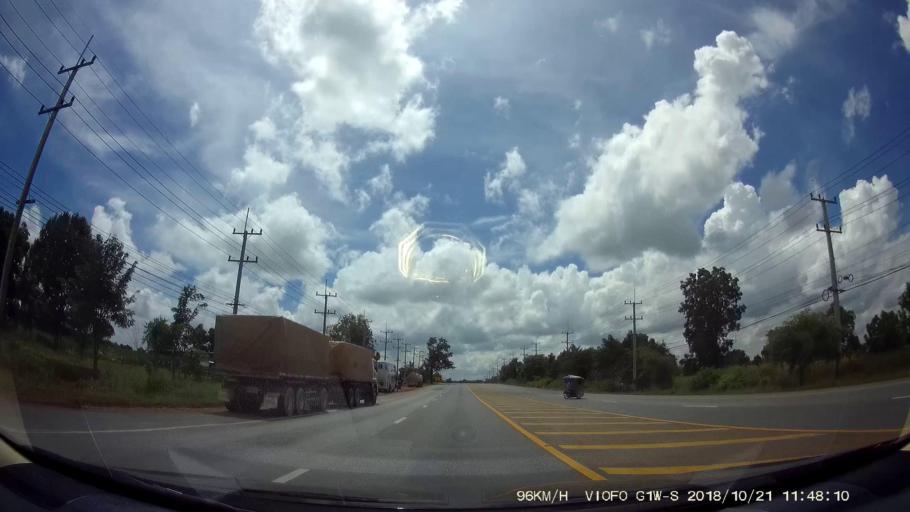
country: TH
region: Chaiyaphum
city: Noen Sa-nga
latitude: 15.6511
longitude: 101.9509
